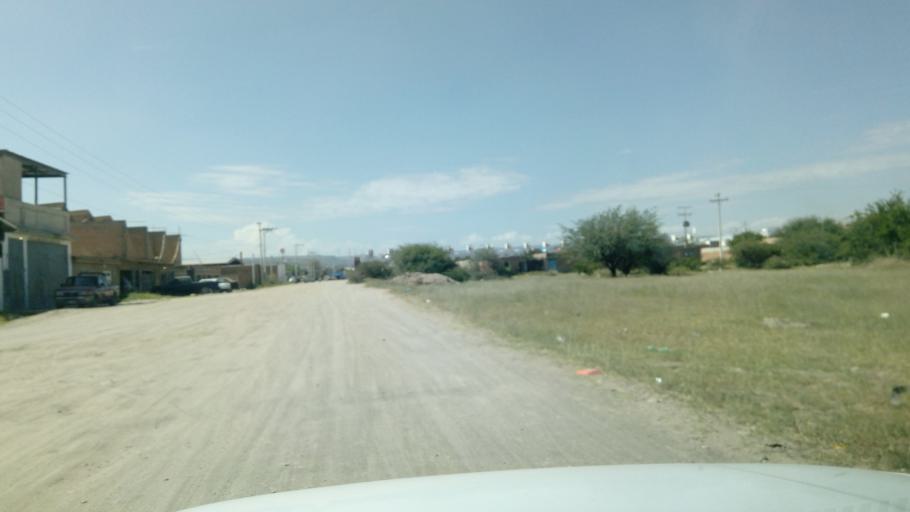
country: MX
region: Durango
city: Victoria de Durango
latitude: 23.9898
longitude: -104.6854
